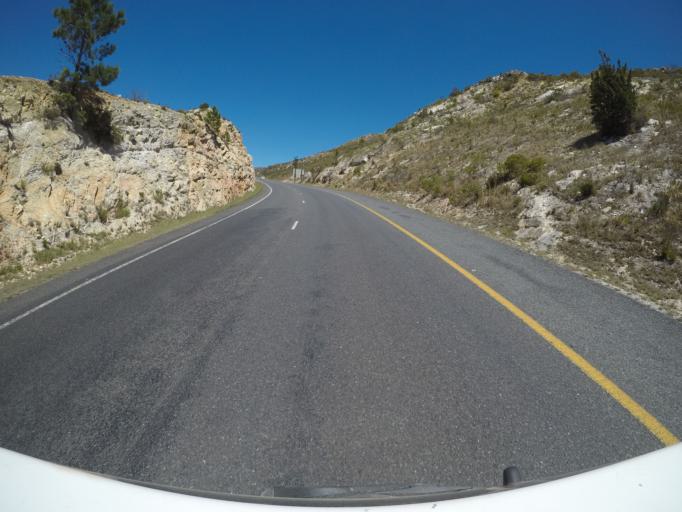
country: ZA
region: Western Cape
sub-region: Overberg District Municipality
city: Grabouw
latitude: -34.2180
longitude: 19.1872
